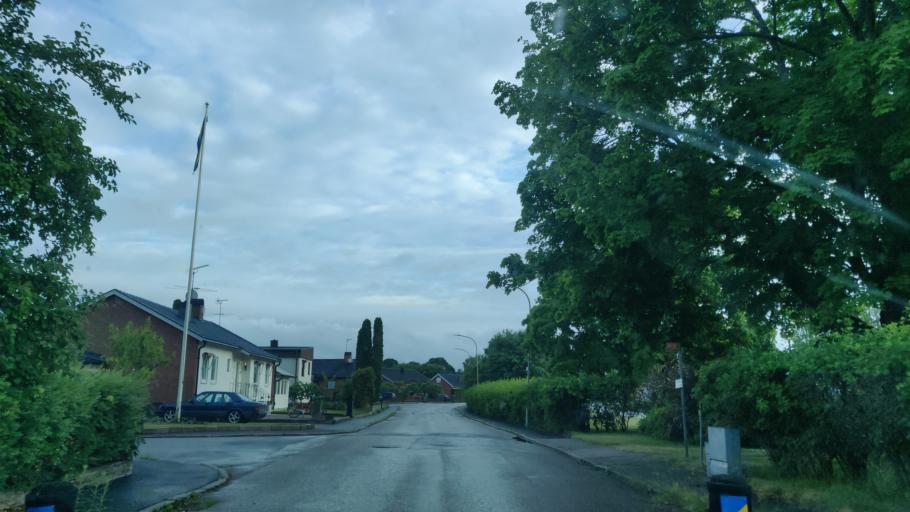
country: SE
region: OErebro
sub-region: Orebro Kommun
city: Orebro
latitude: 59.2959
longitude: 15.1703
